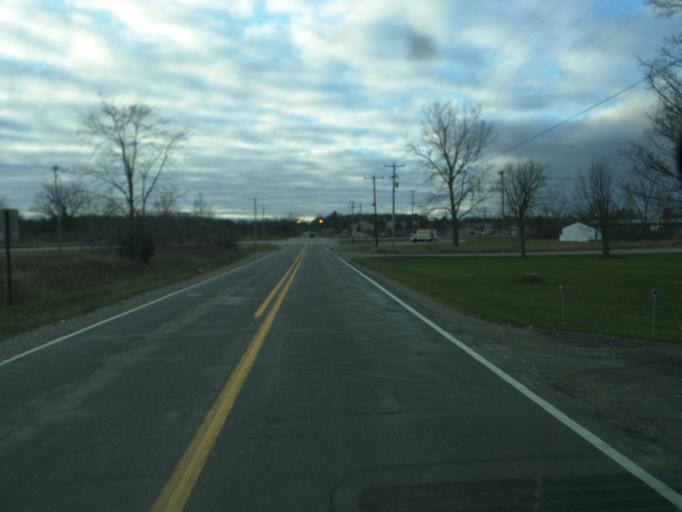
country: US
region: Michigan
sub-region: Eaton County
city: Dimondale
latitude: 42.6552
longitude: -84.6030
